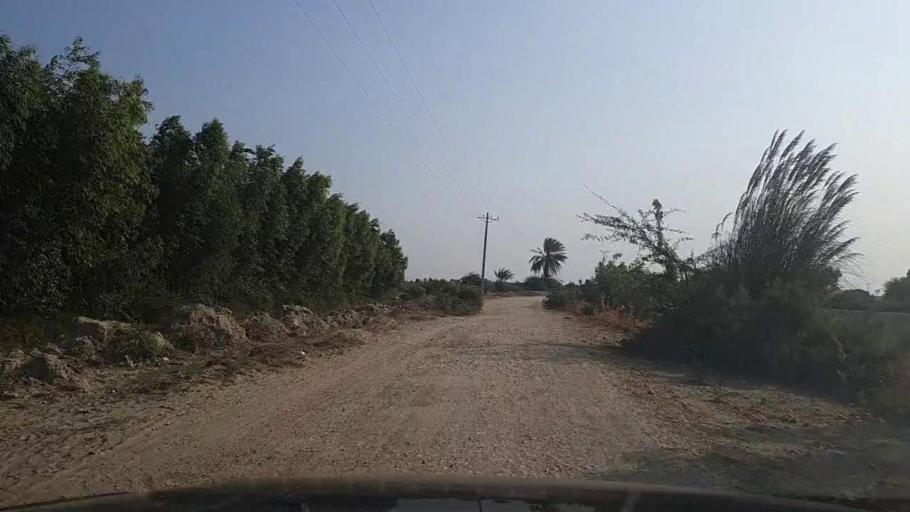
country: PK
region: Sindh
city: Mirpur Sakro
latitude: 24.6327
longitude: 67.7564
